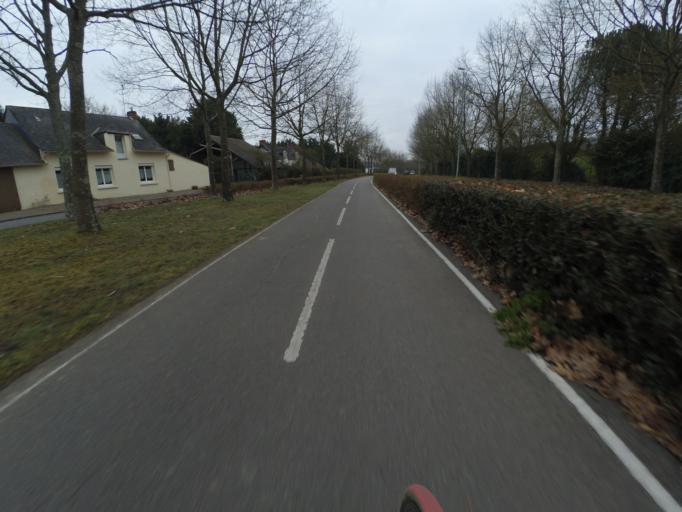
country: FR
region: Pays de la Loire
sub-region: Departement de la Loire-Atlantique
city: Carquefou
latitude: 47.2873
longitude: -1.4842
